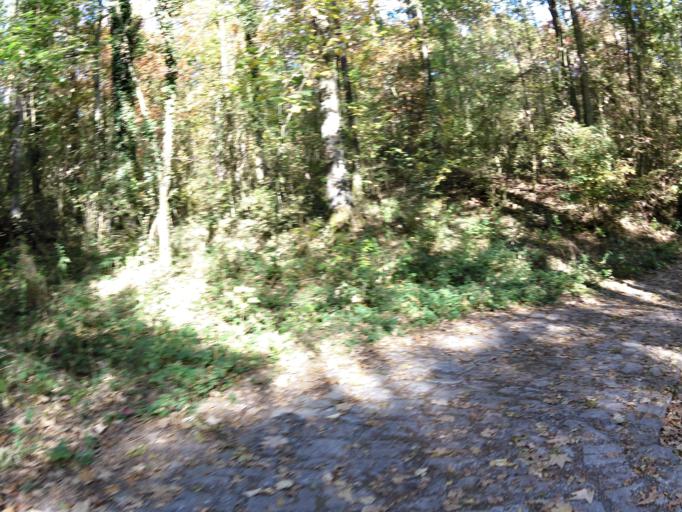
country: DE
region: Bavaria
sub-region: Regierungsbezirk Unterfranken
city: Eibelstadt
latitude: 49.7289
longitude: 9.9805
